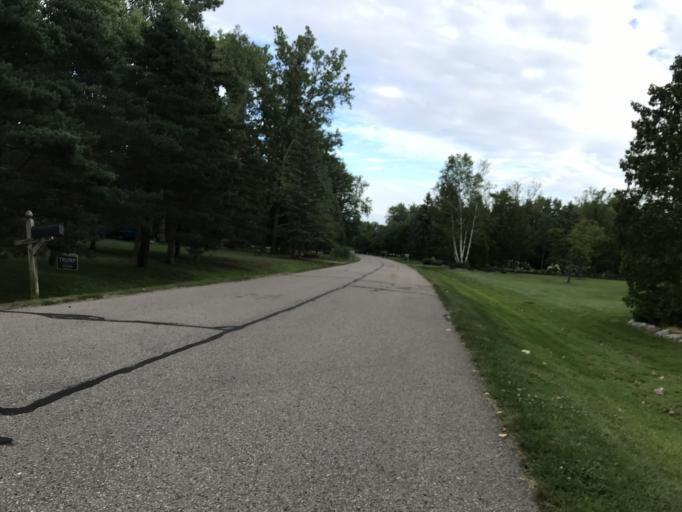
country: US
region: Michigan
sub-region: Oakland County
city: Farmington Hills
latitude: 42.4826
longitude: -83.3445
